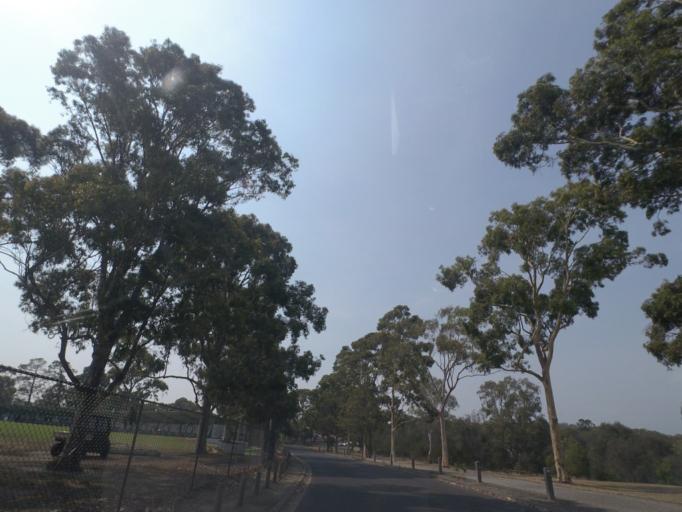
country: AU
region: Victoria
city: Abbotsford
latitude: -37.7956
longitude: 145.0100
